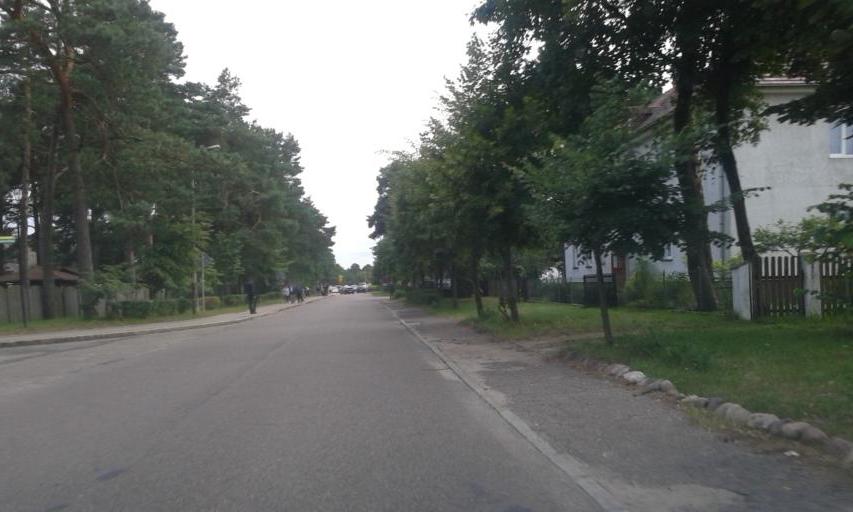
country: PL
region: West Pomeranian Voivodeship
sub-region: Powiat szczecinecki
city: Borne Sulinowo
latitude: 53.5783
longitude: 16.5327
